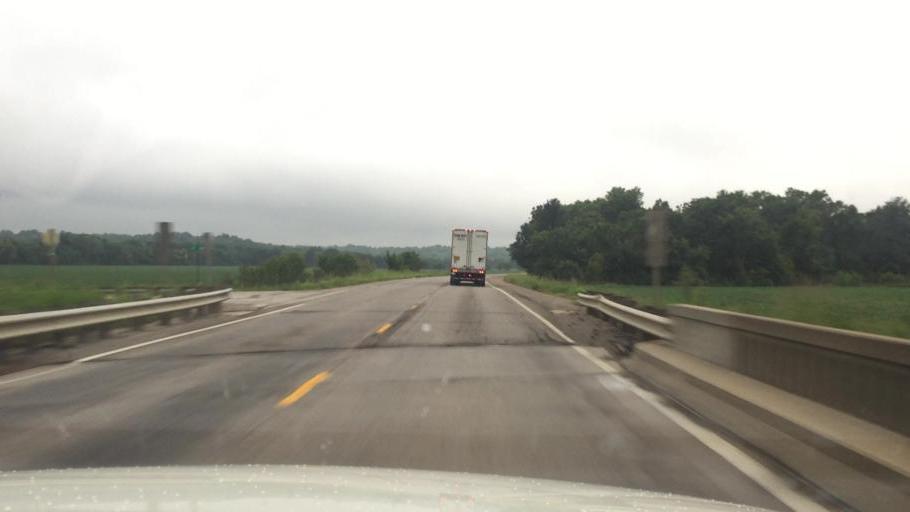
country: US
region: Kansas
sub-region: Montgomery County
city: Cherryvale
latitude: 37.1798
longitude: -95.5773
